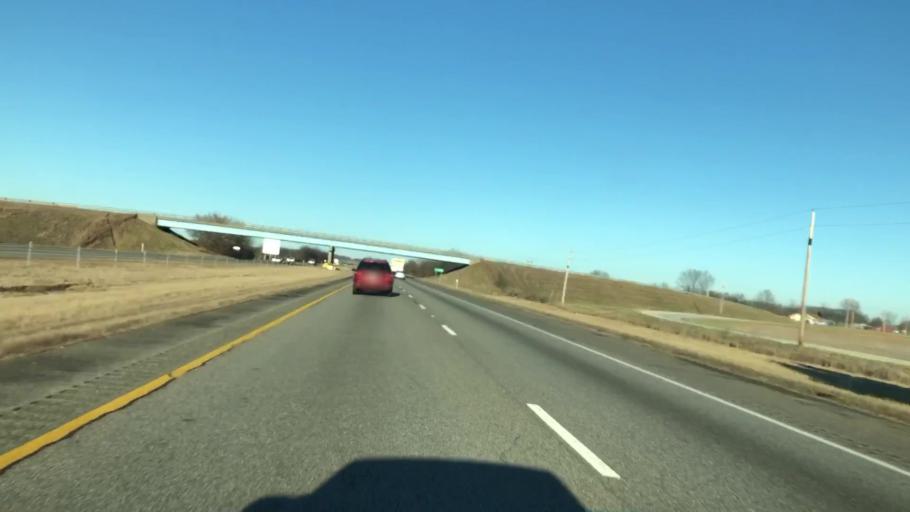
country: US
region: Indiana
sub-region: Johnson County
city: Edinburgh
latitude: 39.3166
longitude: -85.9486
